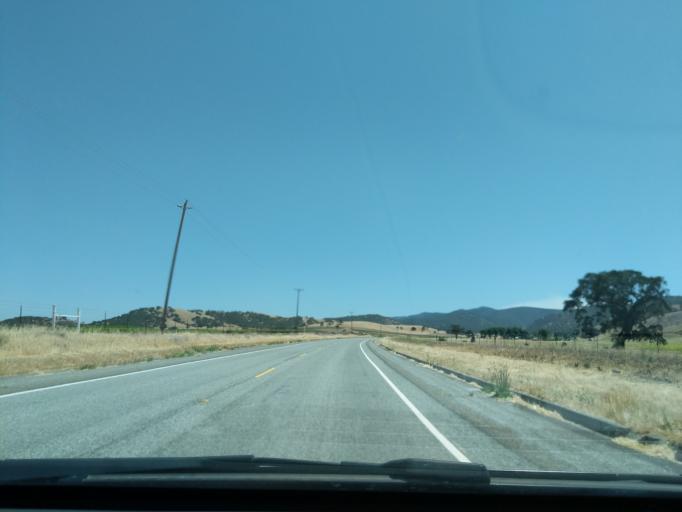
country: US
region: California
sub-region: Monterey County
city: King City
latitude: 36.1490
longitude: -121.1282
